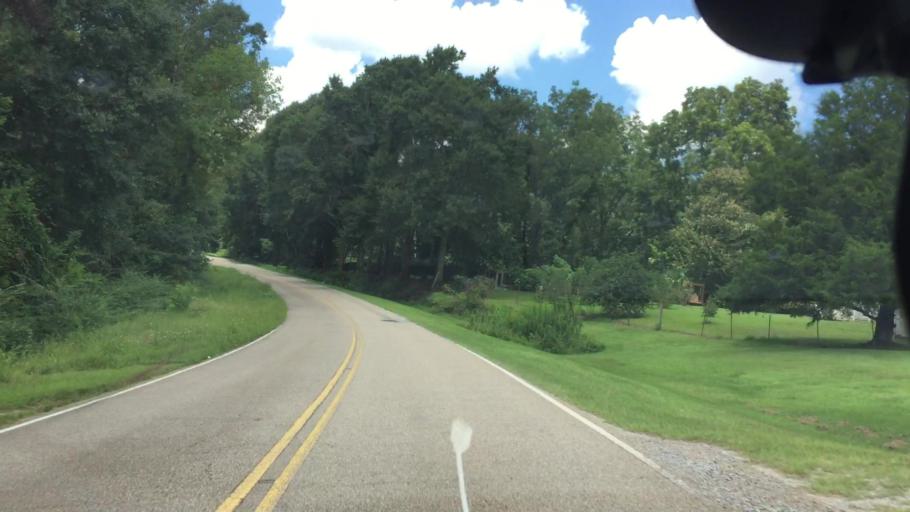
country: US
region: Alabama
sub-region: Coffee County
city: Enterprise
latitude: 31.3993
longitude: -85.8321
